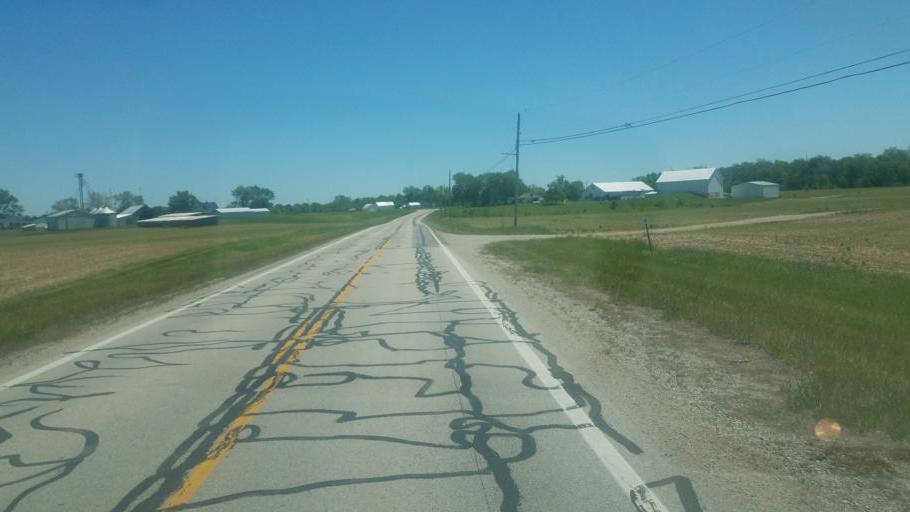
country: US
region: Ohio
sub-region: Darke County
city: Versailles
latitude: 40.2372
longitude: -84.5082
